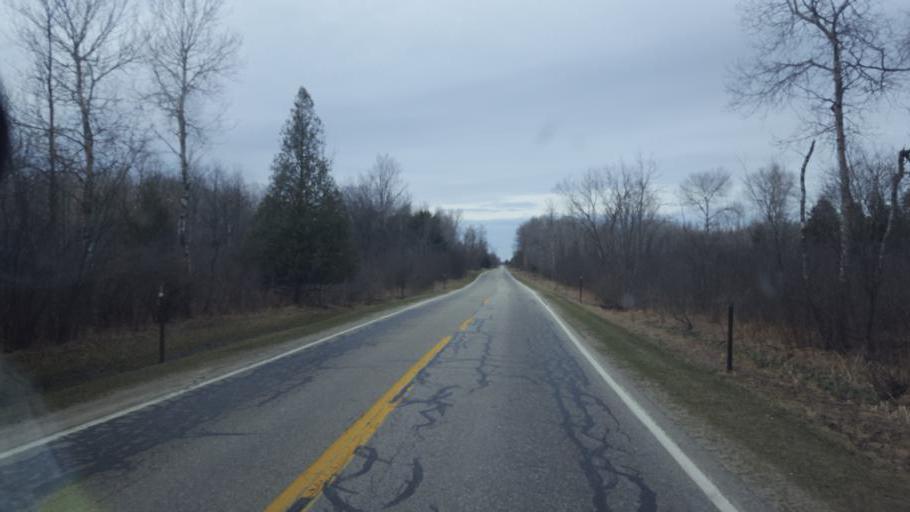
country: US
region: Michigan
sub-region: Montcalm County
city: Edmore
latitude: 43.5112
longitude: -85.0059
